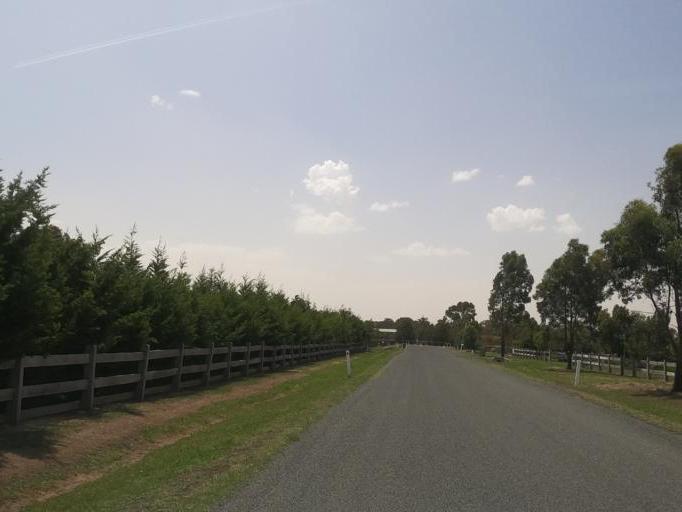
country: AU
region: Victoria
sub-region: Hume
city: Craigieburn
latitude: -37.5598
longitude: 144.8912
